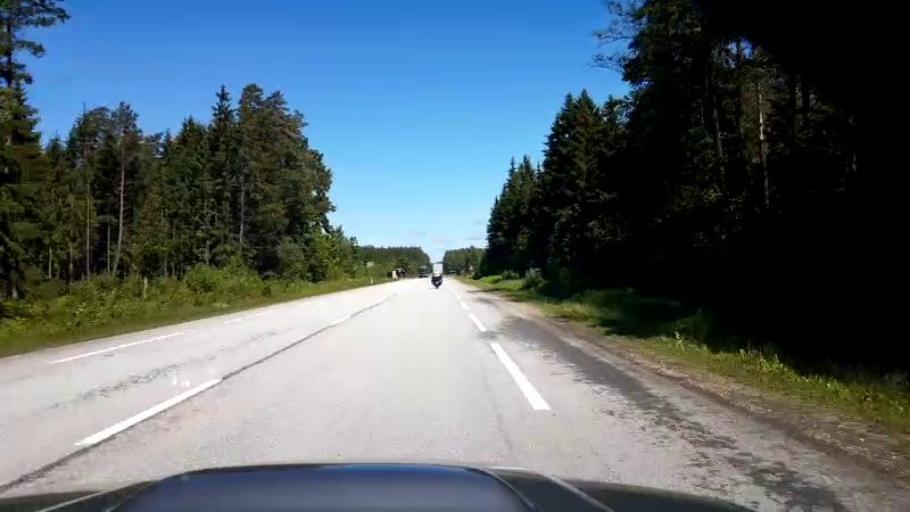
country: LV
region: Saulkrastu
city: Saulkrasti
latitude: 57.4244
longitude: 24.4291
